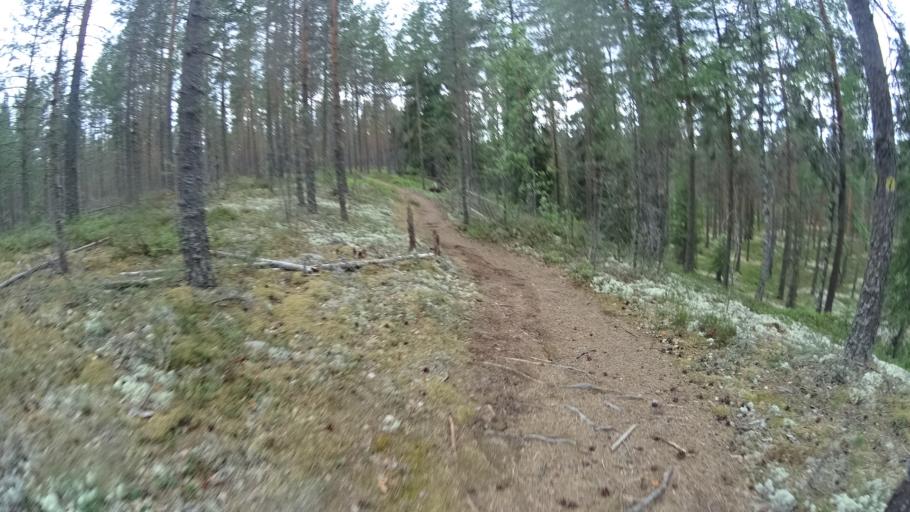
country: FI
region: Satakunta
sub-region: Pohjois-Satakunta
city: Jaemijaervi
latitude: 61.7697
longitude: 22.7776
